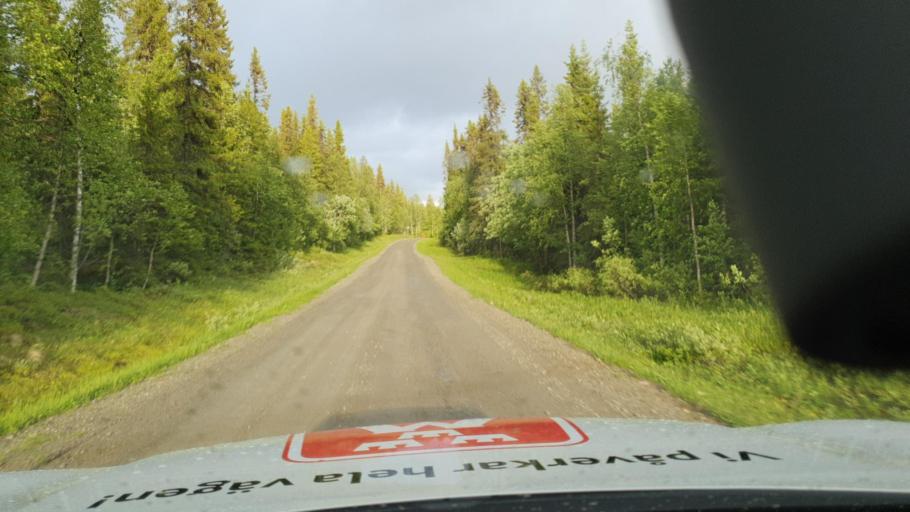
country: SE
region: Vaesterbotten
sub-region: Storumans Kommun
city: Storuman
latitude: 64.7867
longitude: 17.0229
